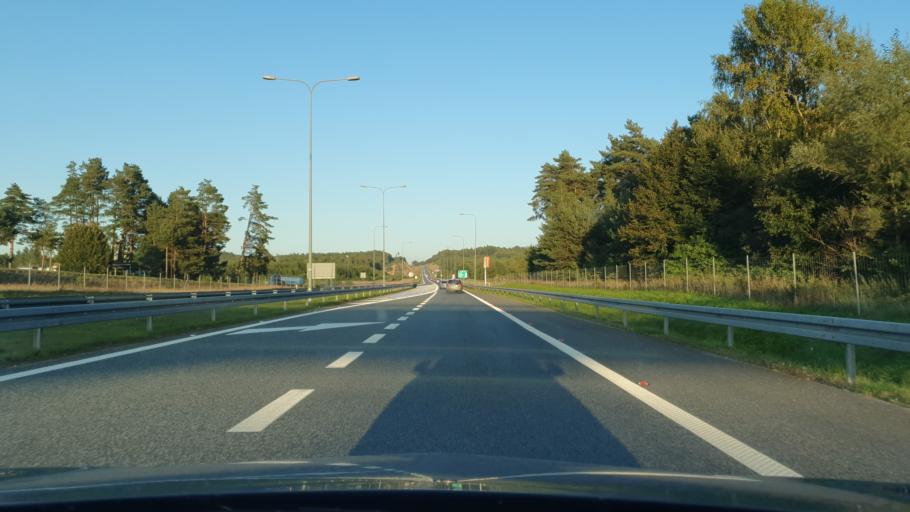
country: PL
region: Pomeranian Voivodeship
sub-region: Powiat slupski
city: Kobylnica
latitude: 54.4257
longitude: 17.0164
